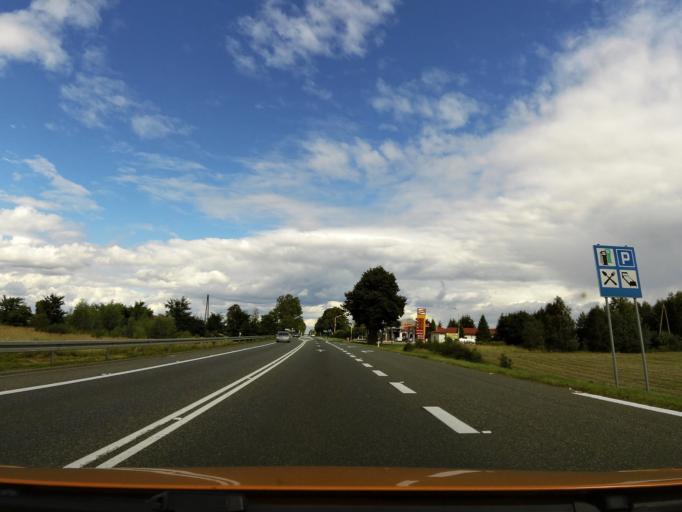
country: PL
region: West Pomeranian Voivodeship
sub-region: Powiat goleniowski
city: Osina
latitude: 53.6416
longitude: 15.0510
